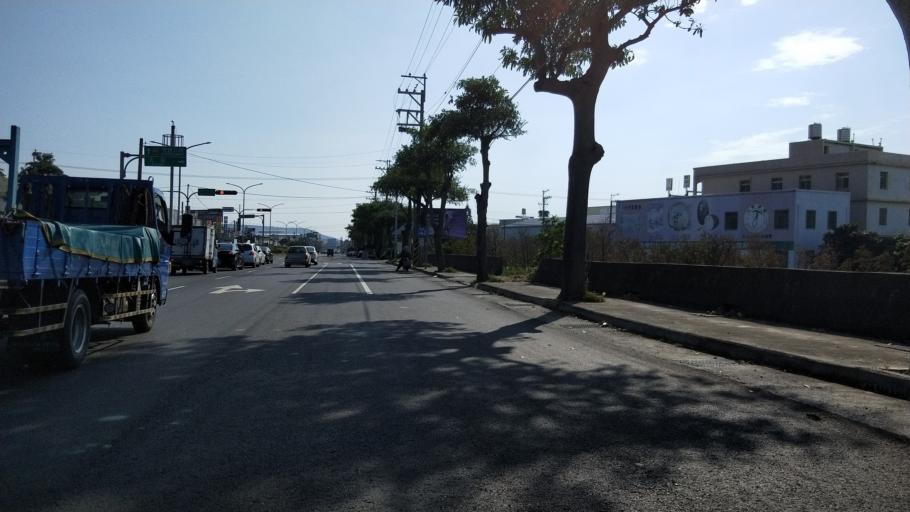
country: TW
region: Taiwan
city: Fengyuan
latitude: 24.3665
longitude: 120.6419
